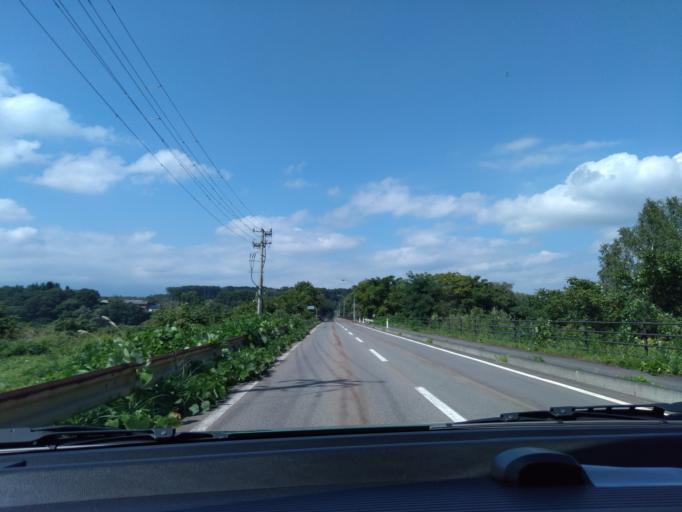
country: JP
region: Iwate
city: Shizukuishi
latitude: 39.6648
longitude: 140.9825
